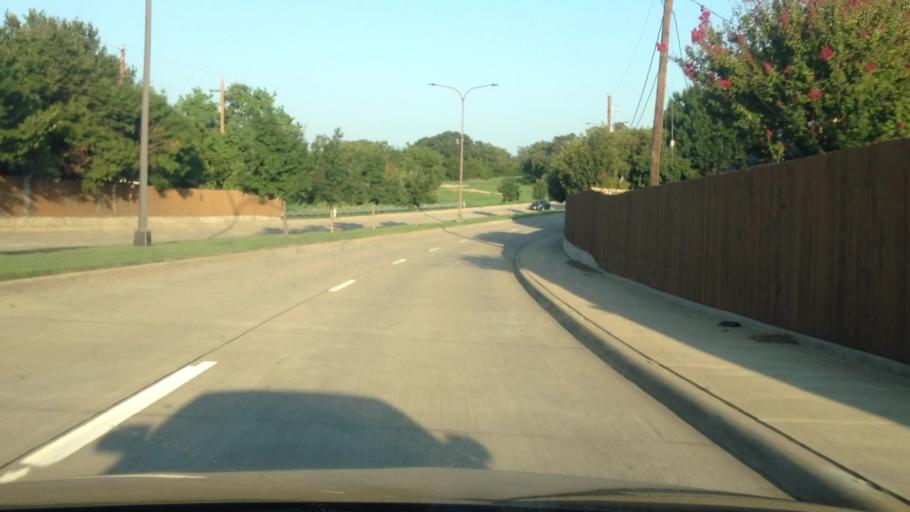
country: US
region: Texas
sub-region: Tarrant County
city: Dalworthington Gardens
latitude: 32.6821
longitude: -97.1694
